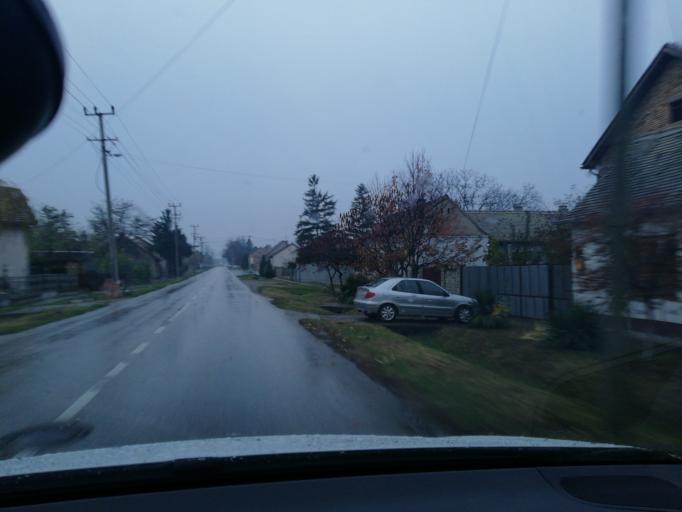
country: RS
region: Autonomna Pokrajina Vojvodina
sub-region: Sremski Okrug
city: Ruma
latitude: 45.0034
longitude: 19.8416
